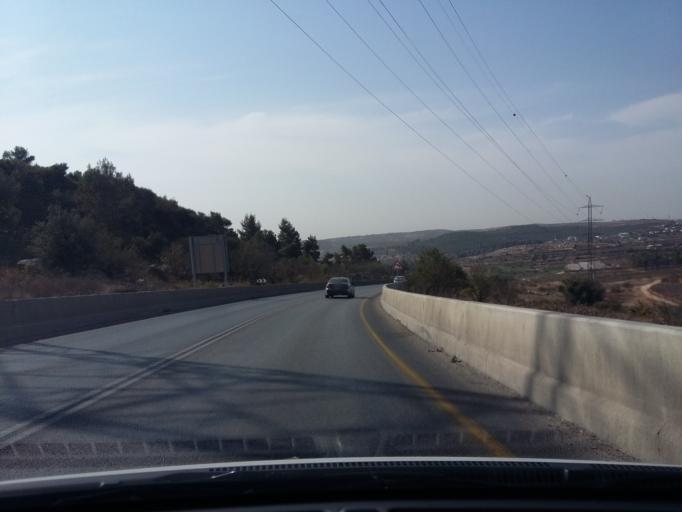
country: PS
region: West Bank
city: Shuyukh al `Arrub
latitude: 31.6429
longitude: 35.1315
